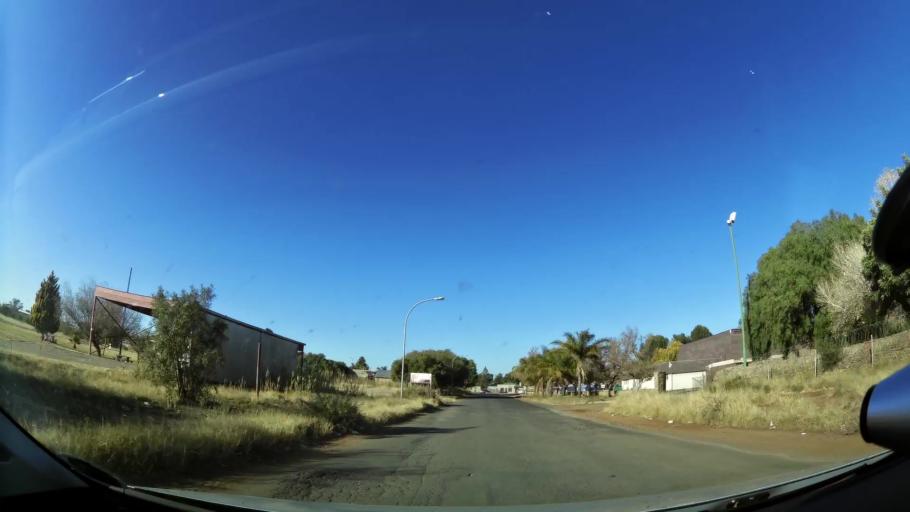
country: ZA
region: Northern Cape
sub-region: Frances Baard District Municipality
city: Kimberley
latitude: -28.7427
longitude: 24.7431
